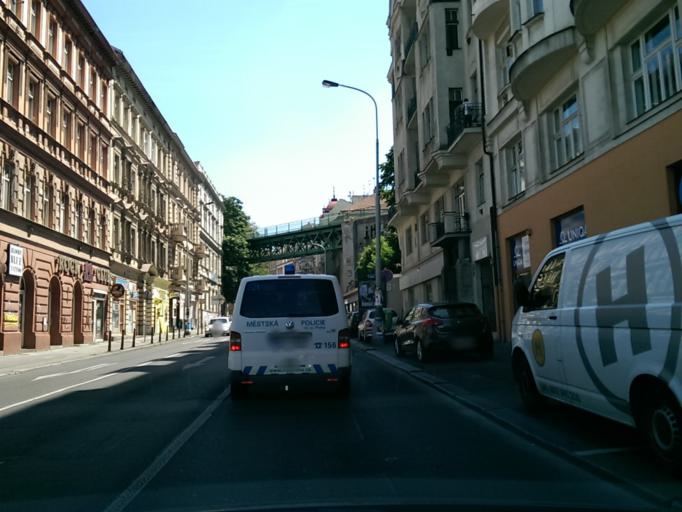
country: CZ
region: Praha
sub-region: Praha 8
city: Karlin
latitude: 50.0872
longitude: 14.4435
